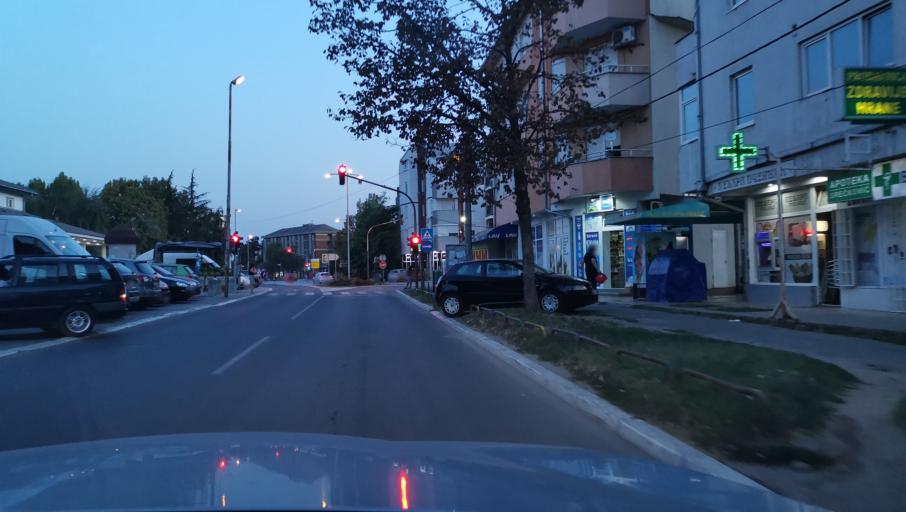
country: RS
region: Central Serbia
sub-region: Belgrade
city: Obrenovac
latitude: 44.6609
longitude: 20.2039
